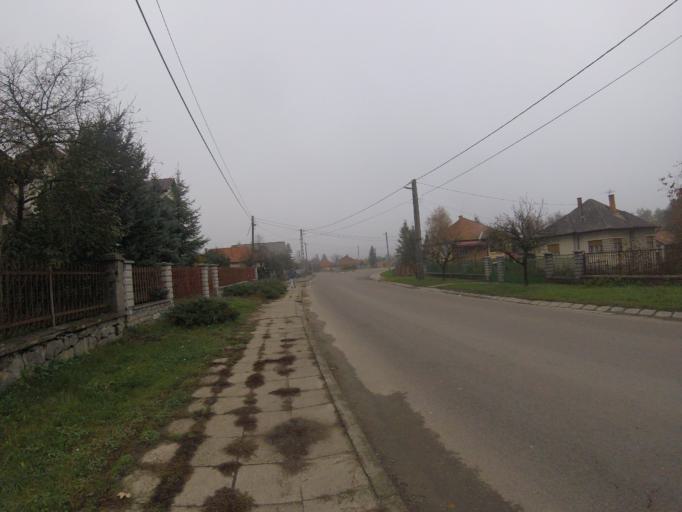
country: HU
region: Heves
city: Szilvasvarad
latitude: 48.1837
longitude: 20.4816
